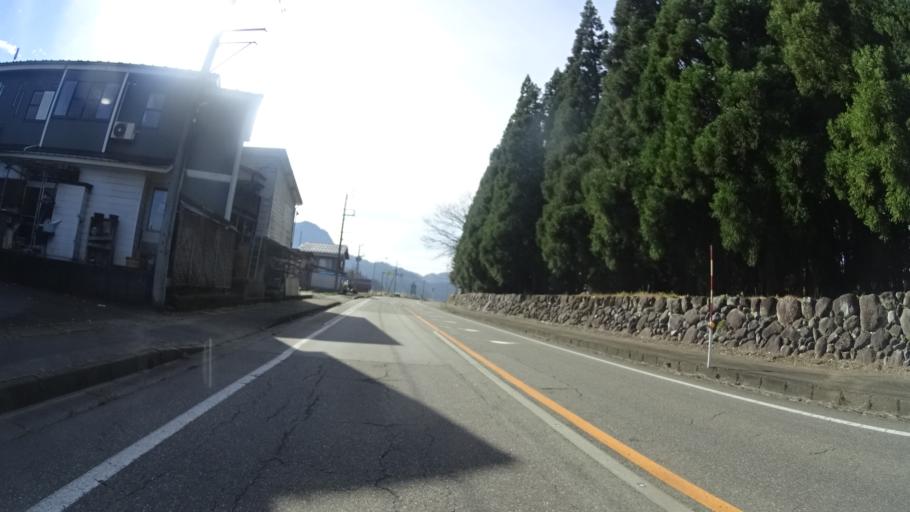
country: JP
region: Niigata
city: Muikamachi
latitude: 37.1299
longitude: 138.9487
